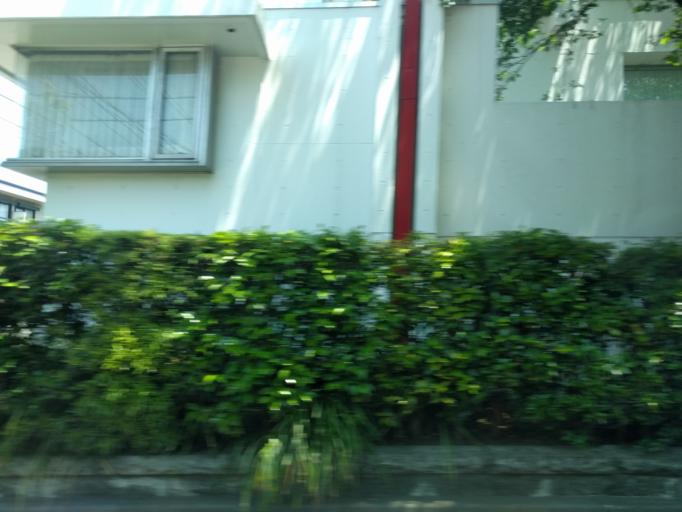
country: JP
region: Tokyo
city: Chofugaoka
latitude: 35.6445
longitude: 139.5965
